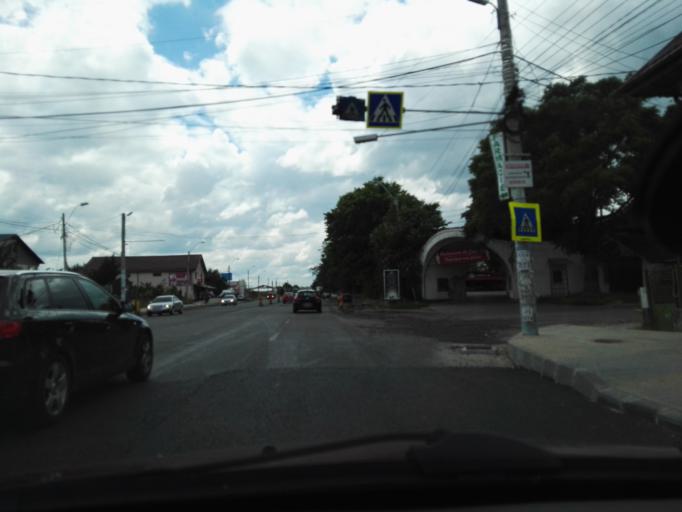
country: RO
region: Ilfov
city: Prim Decembrie
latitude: 44.2854
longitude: 26.0600
